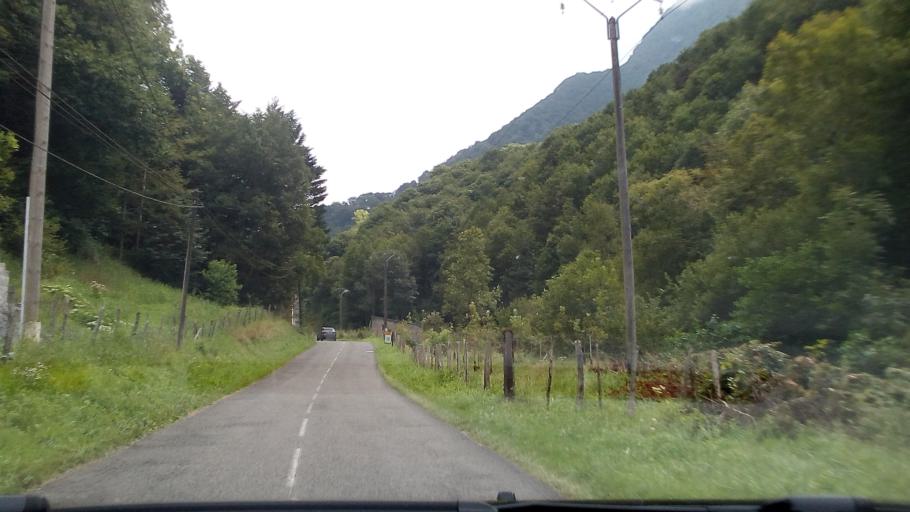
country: FR
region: Aquitaine
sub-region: Departement des Pyrenees-Atlantiques
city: Ogeu-les-Bains
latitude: 43.0784
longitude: -0.5897
